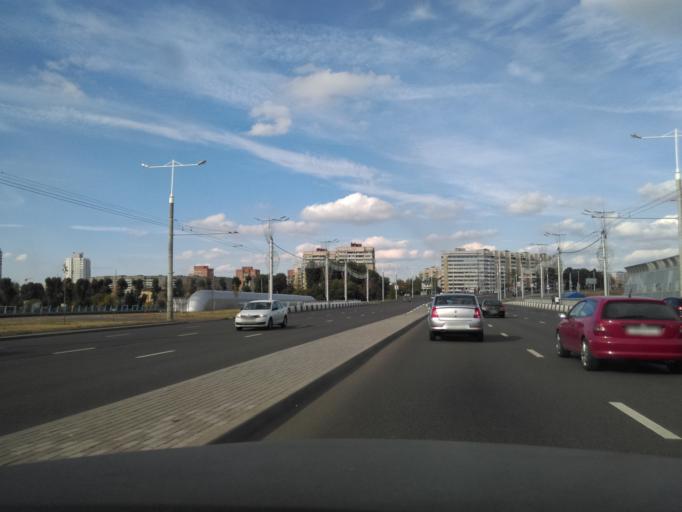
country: BY
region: Minsk
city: Hatava
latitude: 53.8522
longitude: 27.6339
